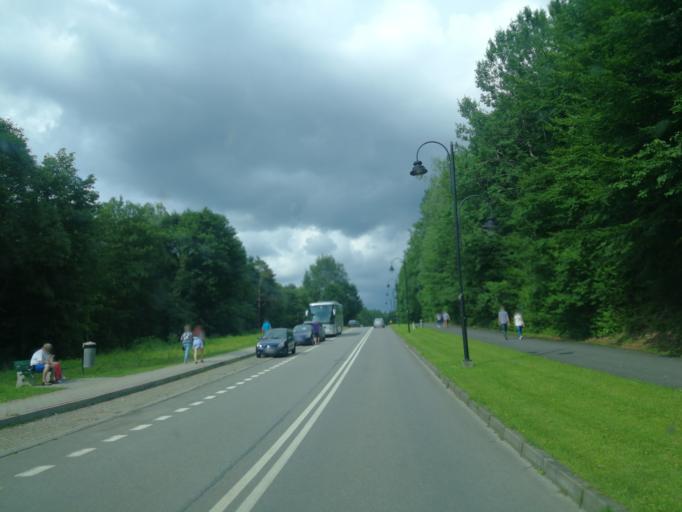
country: PL
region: Subcarpathian Voivodeship
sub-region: Powiat leski
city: Polanczyk
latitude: 49.3752
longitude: 22.4415
